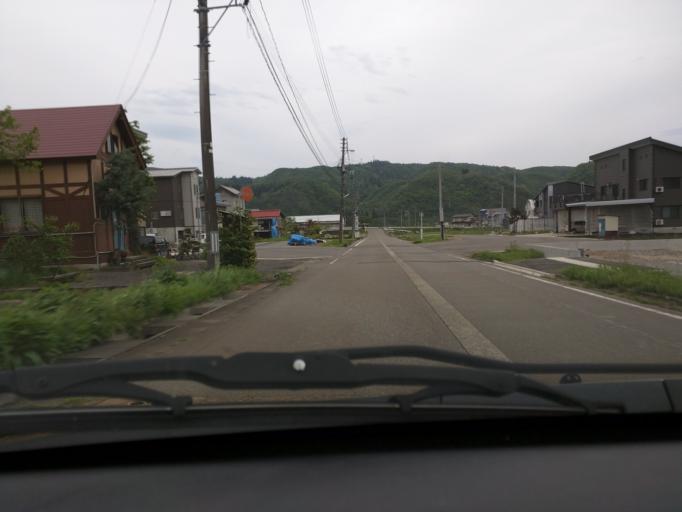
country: JP
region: Niigata
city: Muikamachi
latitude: 37.1934
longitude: 138.9527
